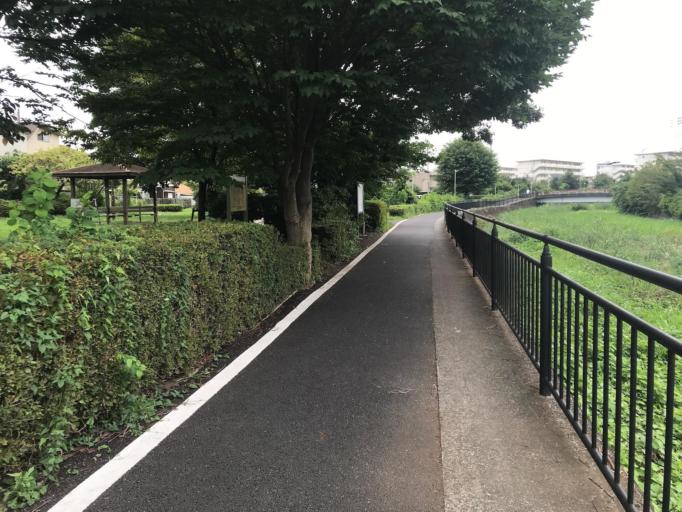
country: JP
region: Tokyo
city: Tanashicho
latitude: 35.7621
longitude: 139.5279
